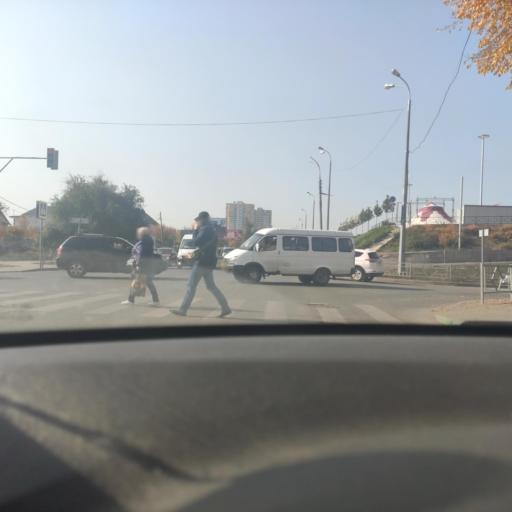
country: RU
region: Samara
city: Samara
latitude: 53.2062
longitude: 50.2037
